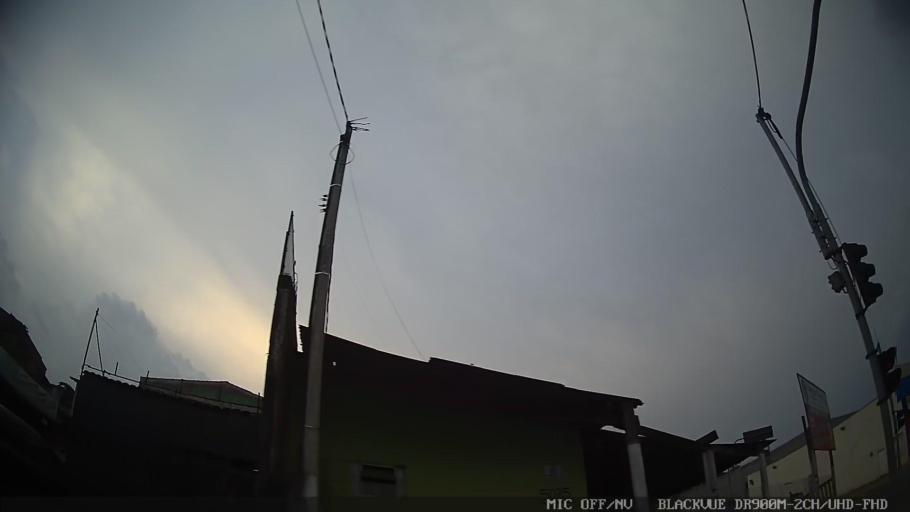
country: BR
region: Sao Paulo
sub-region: Braganca Paulista
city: Braganca Paulista
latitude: -22.9337
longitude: -46.5358
